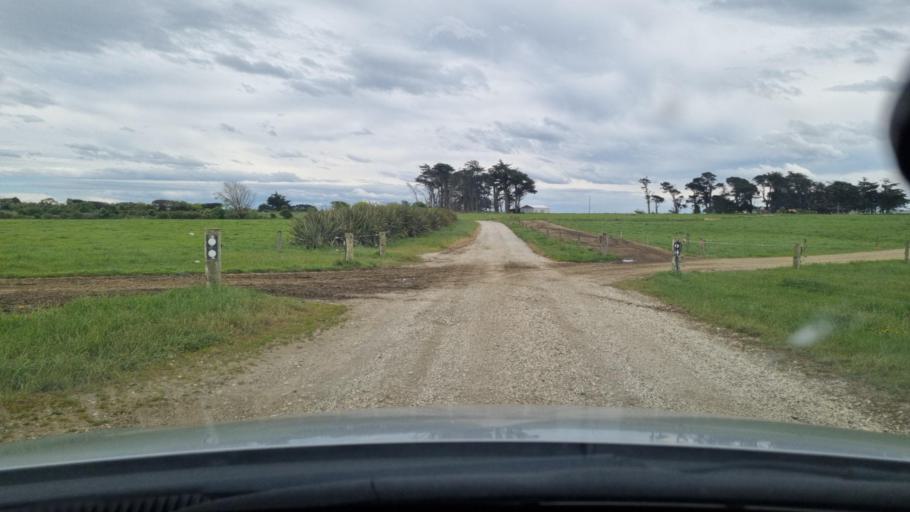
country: NZ
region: Southland
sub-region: Invercargill City
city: Invercargill
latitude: -46.4006
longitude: 168.2613
